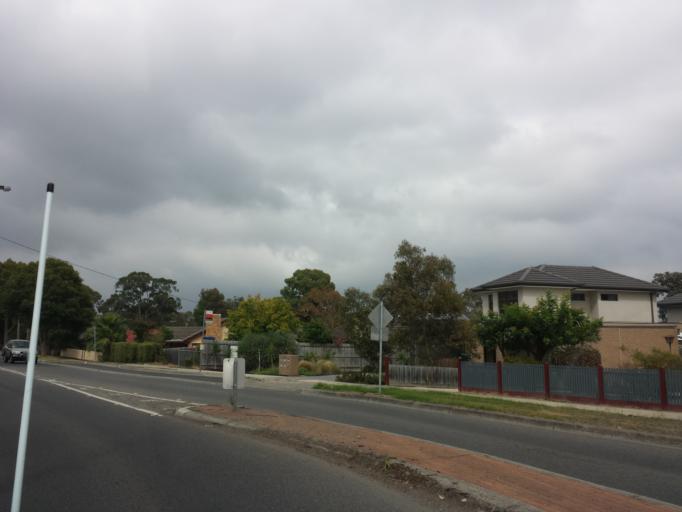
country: AU
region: Victoria
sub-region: Knox
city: Boronia
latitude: -37.8789
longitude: 145.2781
